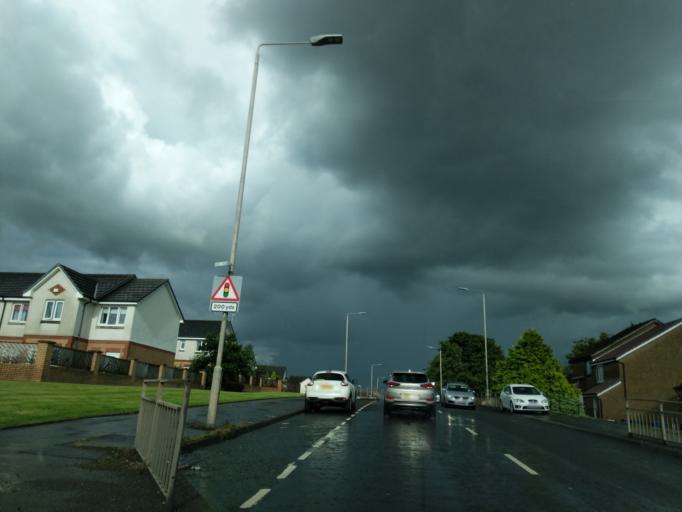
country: GB
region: Scotland
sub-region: East Renfrewshire
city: Barrhead
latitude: 55.8074
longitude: -4.3598
